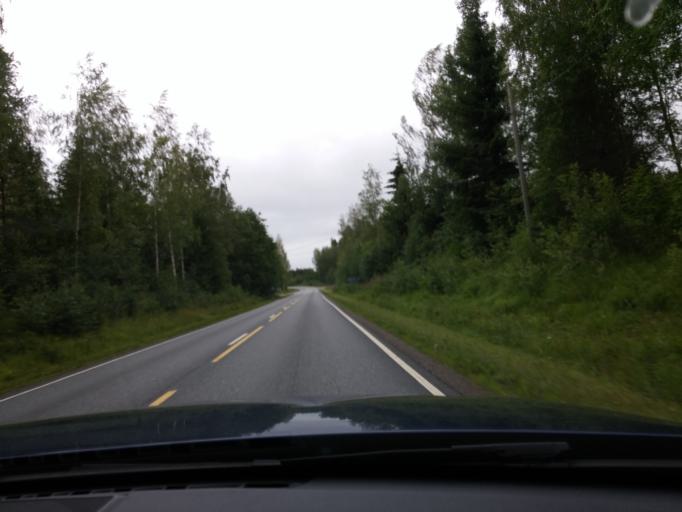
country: FI
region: Central Finland
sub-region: Joutsa
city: Luhanka
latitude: 61.8274
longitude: 25.9017
